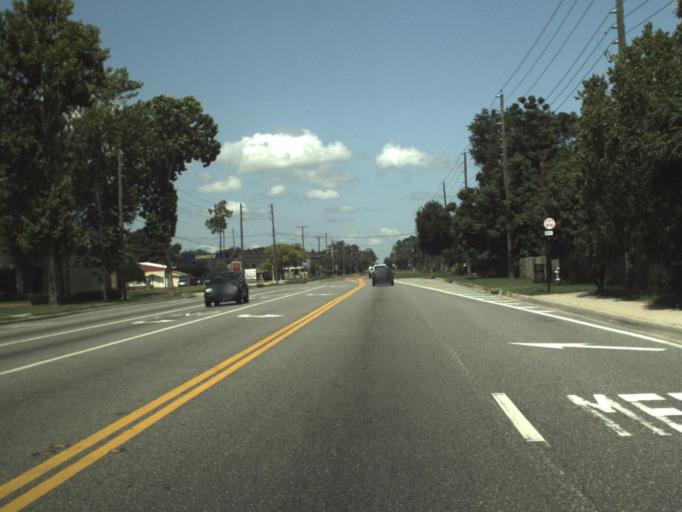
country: US
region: Florida
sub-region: Orange County
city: Conway
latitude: 28.4807
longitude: -81.3108
